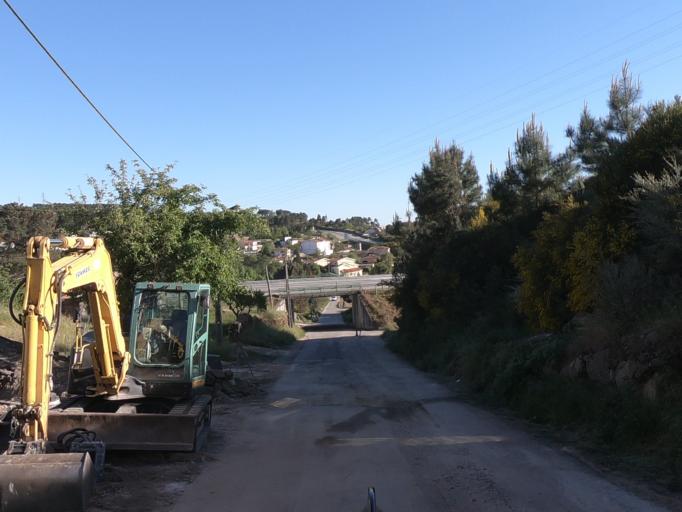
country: PT
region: Vila Real
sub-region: Vila Real
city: Vila Real
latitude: 41.3258
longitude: -7.6941
